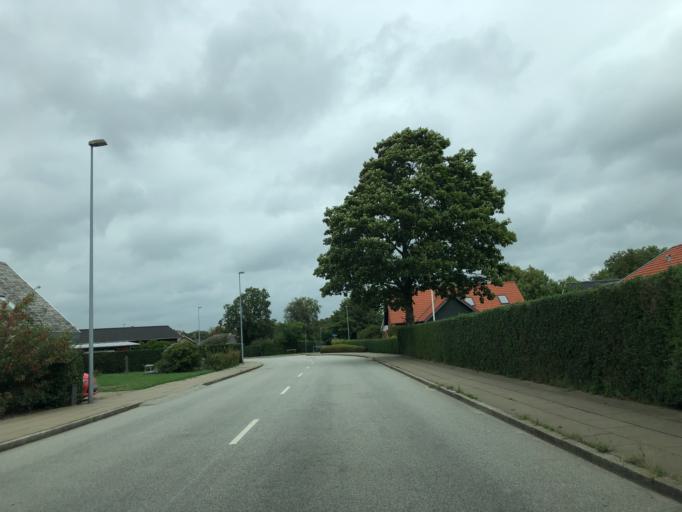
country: DK
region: Central Jutland
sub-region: Herning Kommune
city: Snejbjerg
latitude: 56.1302
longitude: 8.8995
